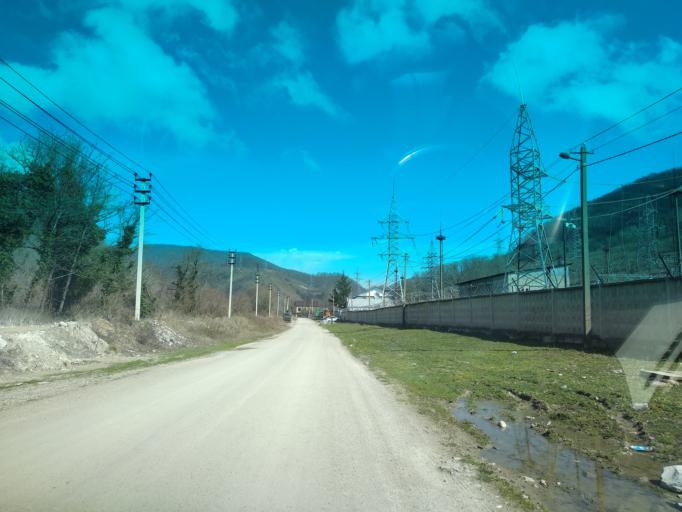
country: RU
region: Krasnodarskiy
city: Shepsi
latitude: 44.0537
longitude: 39.1627
